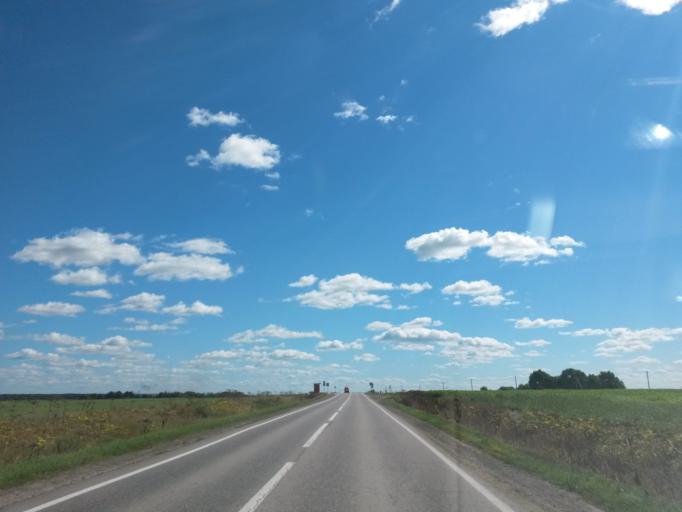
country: RU
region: Jaroslavl
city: Yaroslavl
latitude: 57.7603
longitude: 39.8664
